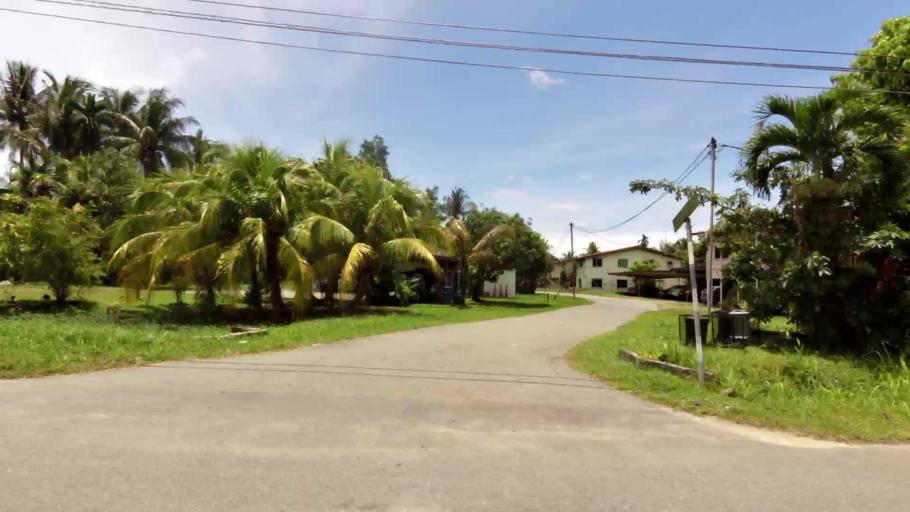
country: BN
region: Belait
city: Kuala Belait
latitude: 4.5828
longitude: 114.2424
